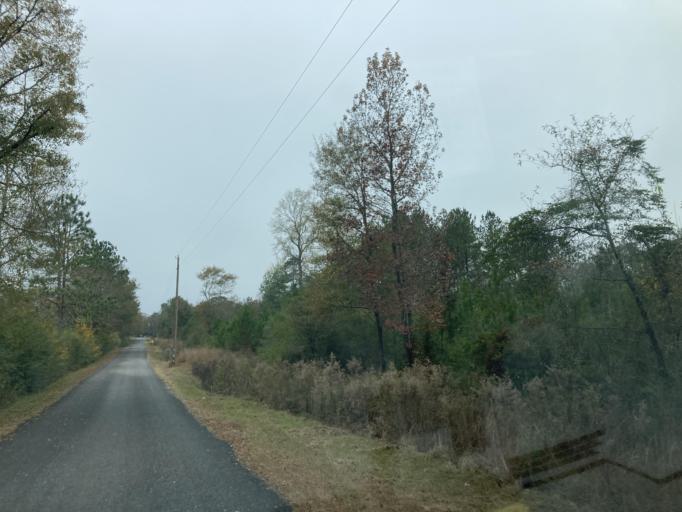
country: US
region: Mississippi
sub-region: Lamar County
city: Lumberton
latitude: 31.0249
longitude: -89.3574
